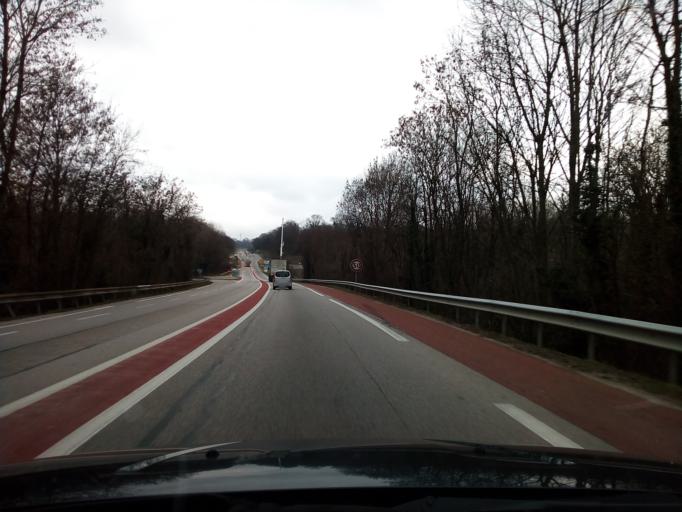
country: FR
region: Rhone-Alpes
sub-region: Departement de l'Isere
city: Moirans
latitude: 45.3349
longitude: 5.5618
